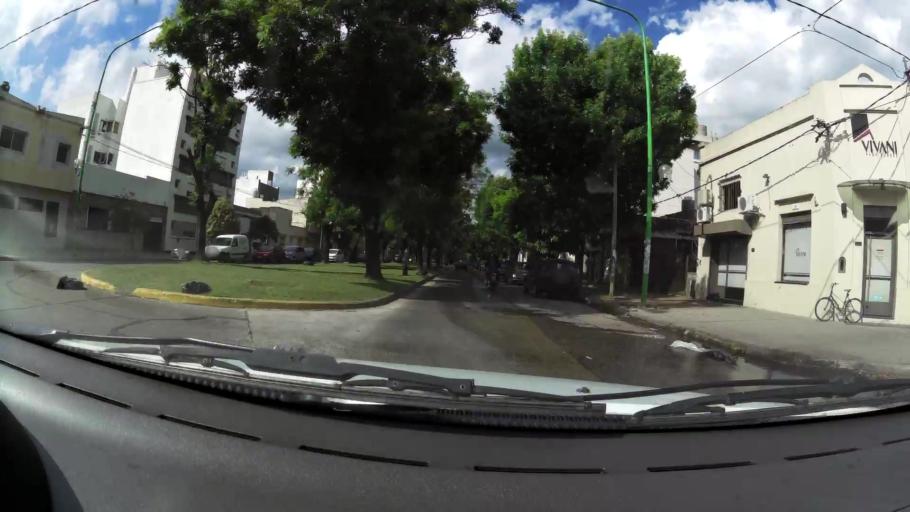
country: AR
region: Buenos Aires
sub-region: Partido de La Plata
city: La Plata
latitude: -34.9194
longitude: -57.9274
